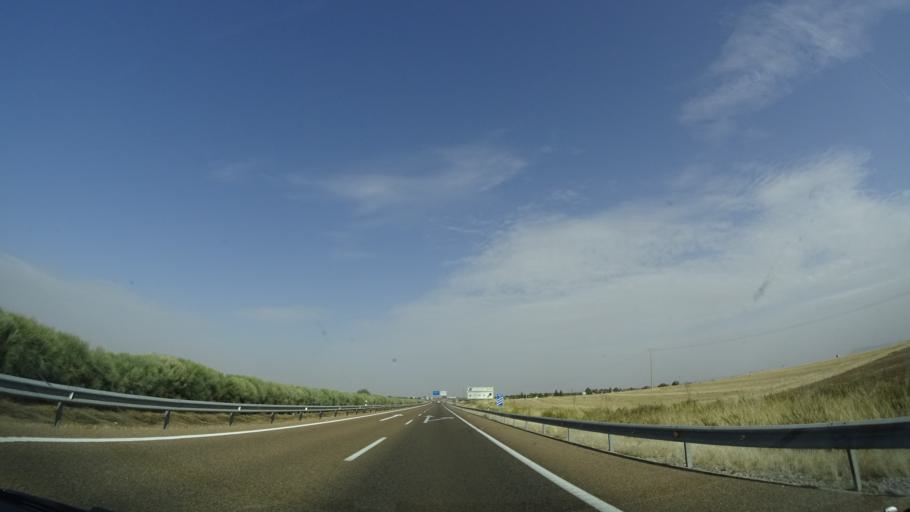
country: ES
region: Extremadura
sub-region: Provincia de Badajoz
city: Villafranca de los Barros
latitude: 38.5173
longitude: -6.3509
